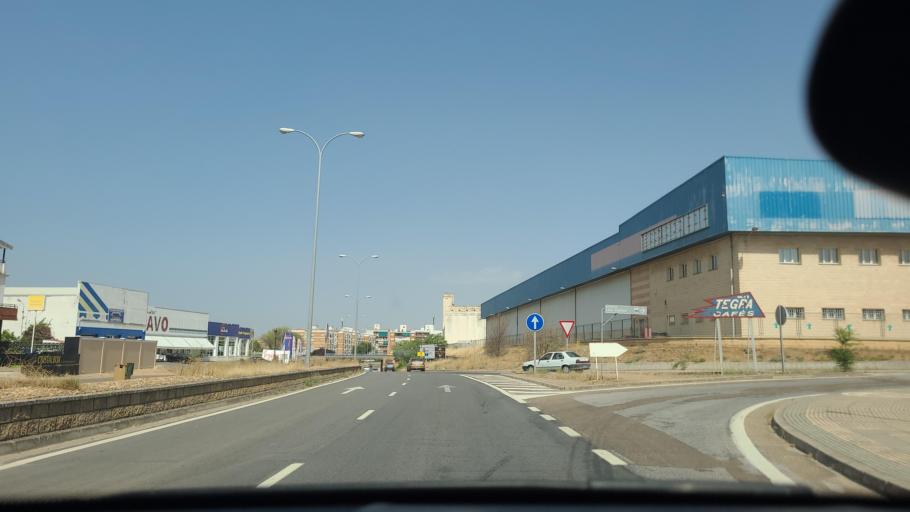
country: ES
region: Extremadura
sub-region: Provincia de Badajoz
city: Zafra
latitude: 38.4211
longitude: -6.4082
